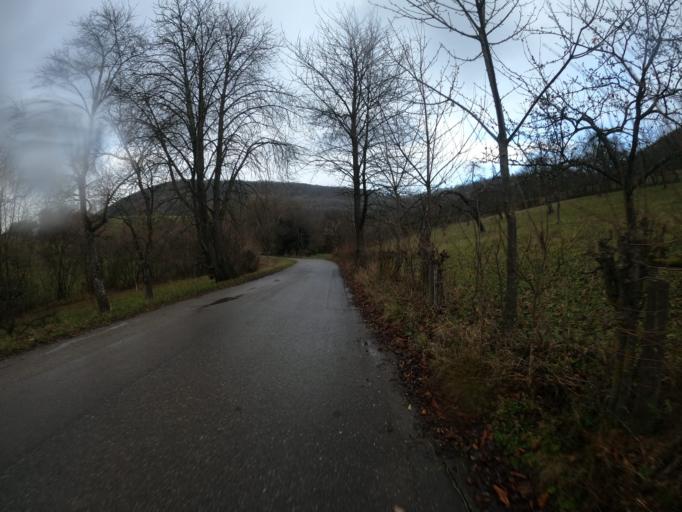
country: DE
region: Baden-Wuerttemberg
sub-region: Regierungsbezirk Stuttgart
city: Donzdorf
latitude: 48.7174
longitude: 9.8593
